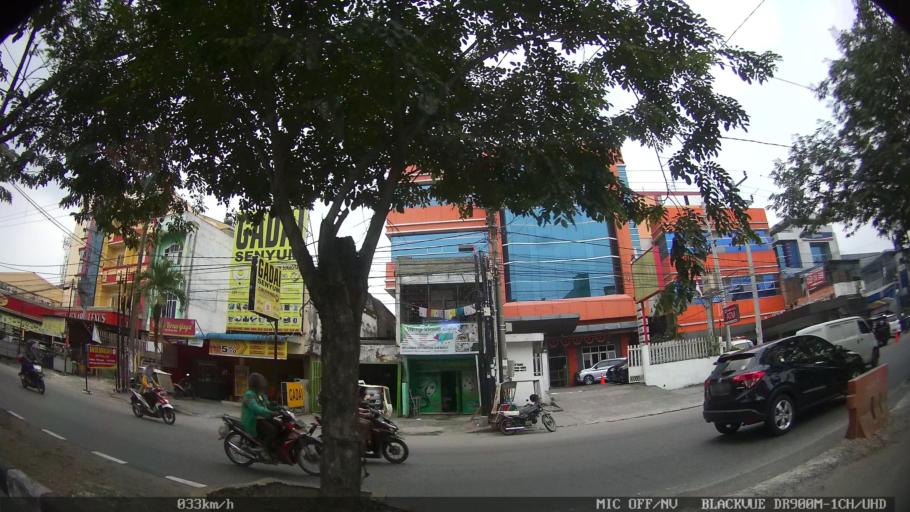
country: ID
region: North Sumatra
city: Medan
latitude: 3.5561
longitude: 98.6951
